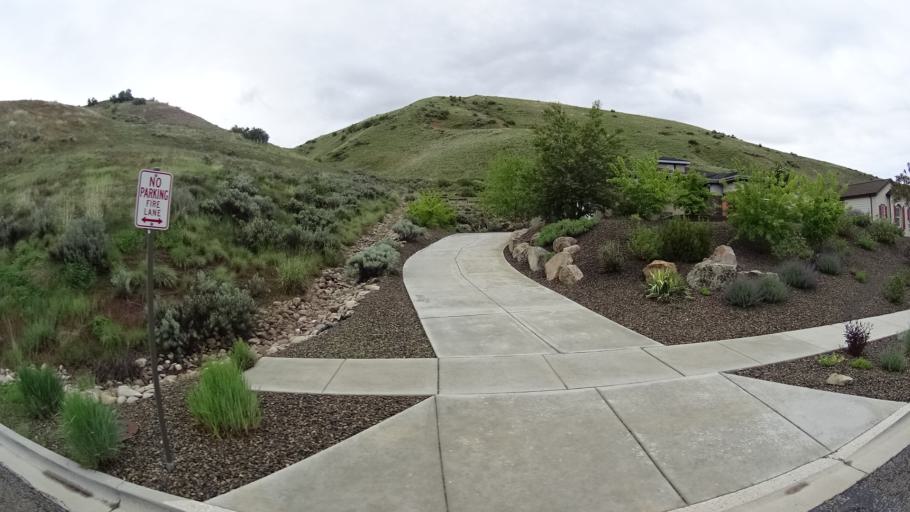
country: US
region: Idaho
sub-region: Ada County
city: Eagle
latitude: 43.7666
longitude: -116.2623
